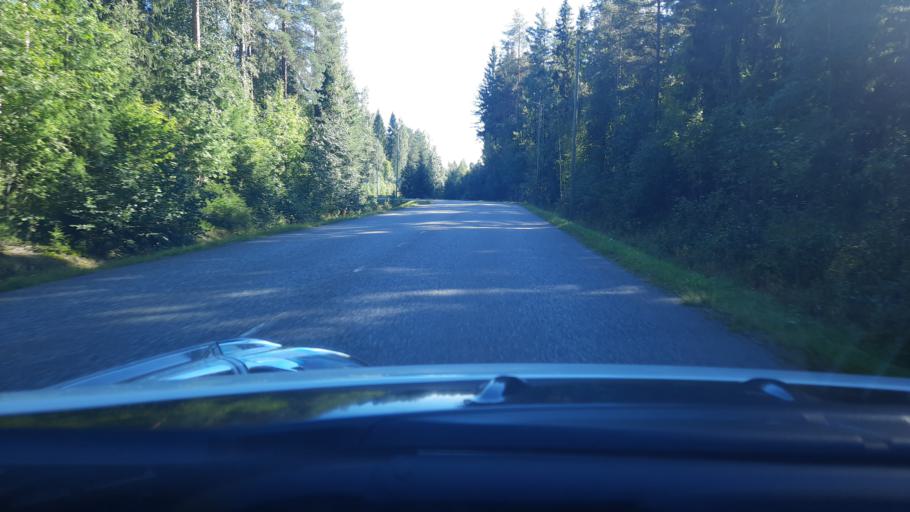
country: FI
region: North Karelia
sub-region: Joensuu
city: Joensuu
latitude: 62.6345
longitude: 29.6996
